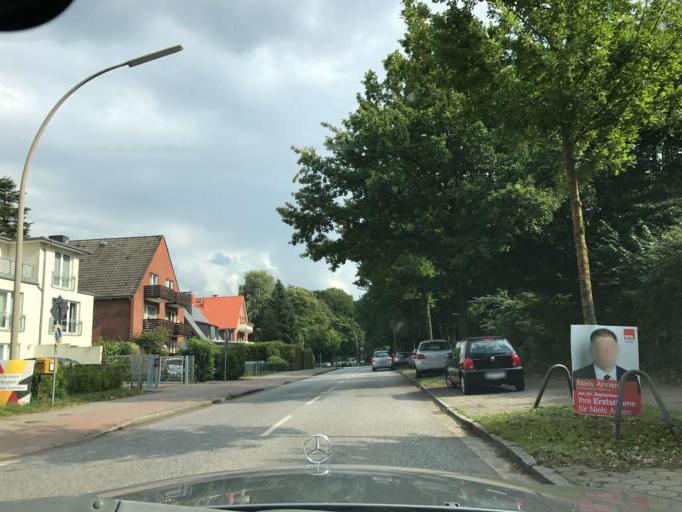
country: DE
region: Hamburg
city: Stellingen
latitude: 53.5993
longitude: 9.9454
